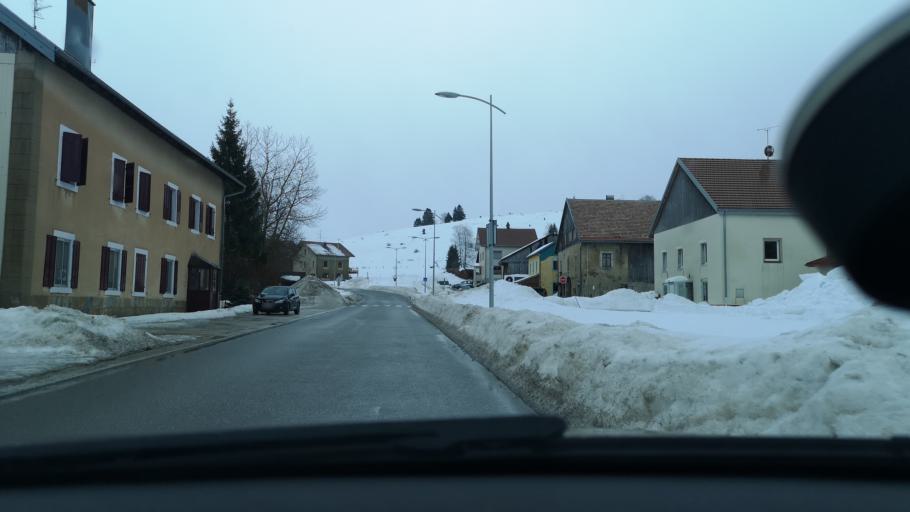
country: FR
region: Franche-Comte
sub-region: Departement du Doubs
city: Les Fourgs
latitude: 46.8334
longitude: 6.4075
